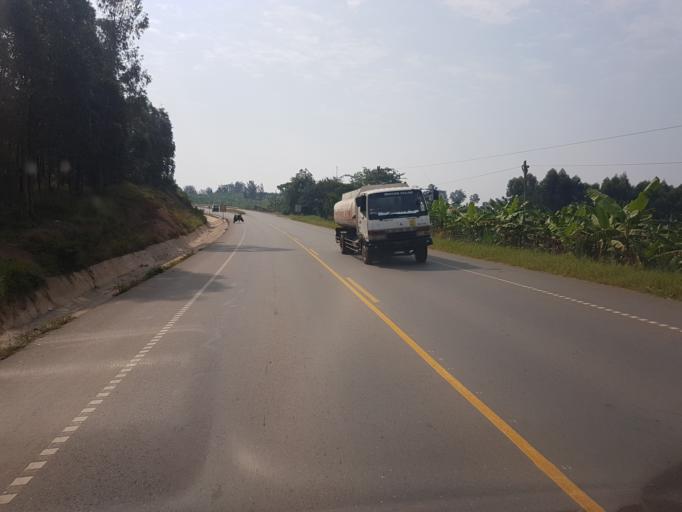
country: UG
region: Western Region
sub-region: Mbarara District
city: Bwizibwera
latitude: -0.6427
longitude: 30.5852
